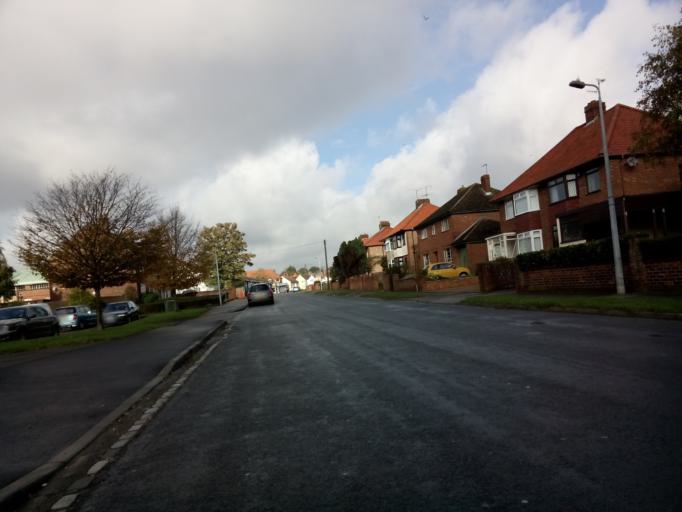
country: GB
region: England
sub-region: Suffolk
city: Bramford
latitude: 52.0774
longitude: 1.1288
